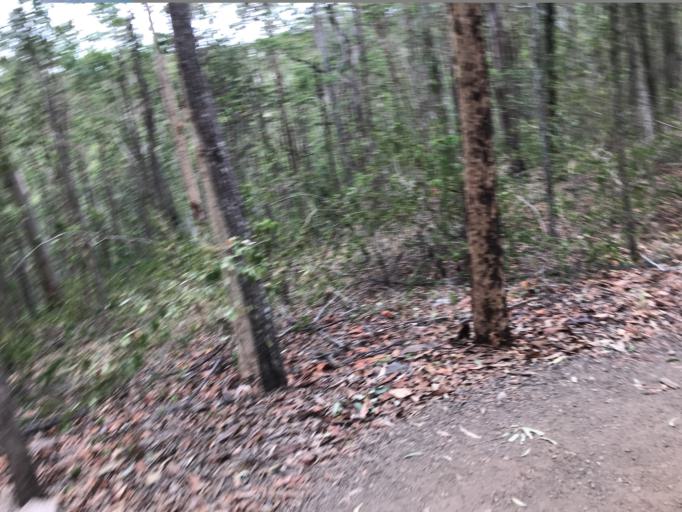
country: AU
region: Queensland
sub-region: Brisbane
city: Taringa
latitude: -27.4695
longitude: 152.9511
